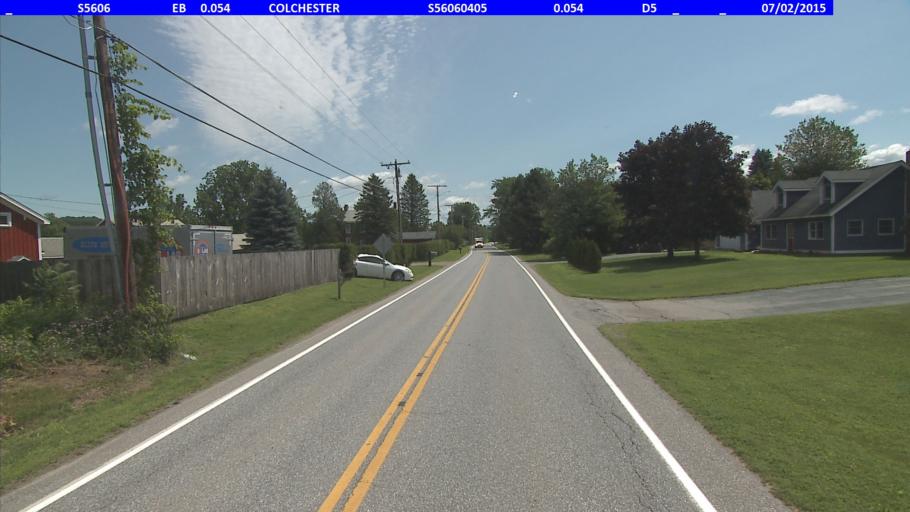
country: US
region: Vermont
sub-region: Chittenden County
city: Burlington
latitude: 44.5512
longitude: -73.2488
